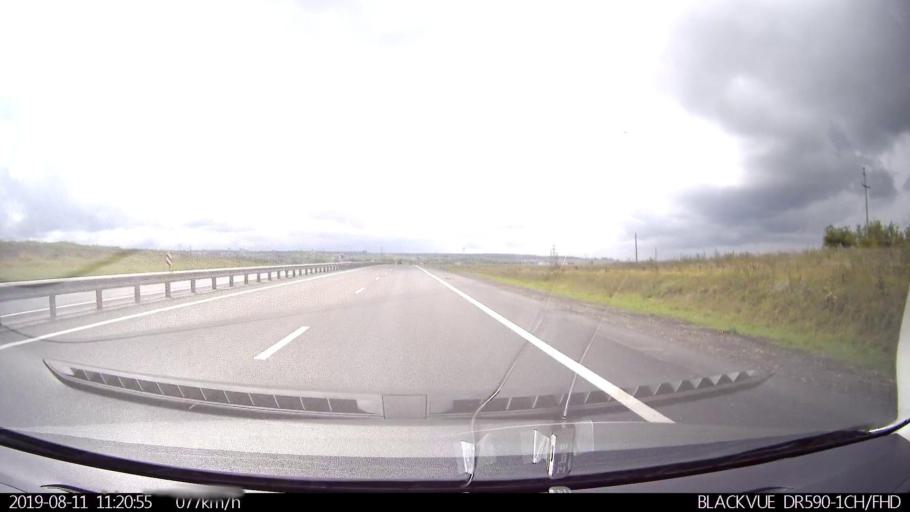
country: RU
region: Ulyanovsk
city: Novoul'yanovsk
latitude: 54.1521
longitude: 48.2642
